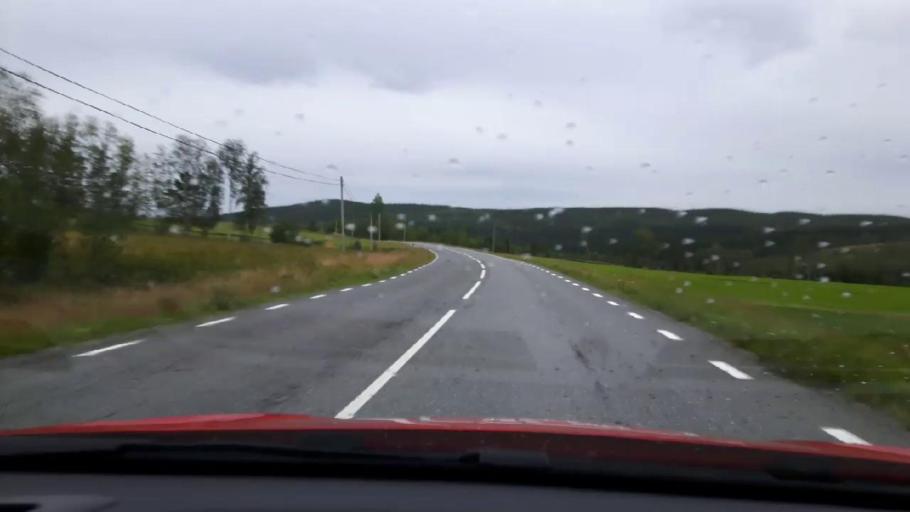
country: SE
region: Jaemtland
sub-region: Are Kommun
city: Jarpen
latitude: 63.4019
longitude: 13.3717
